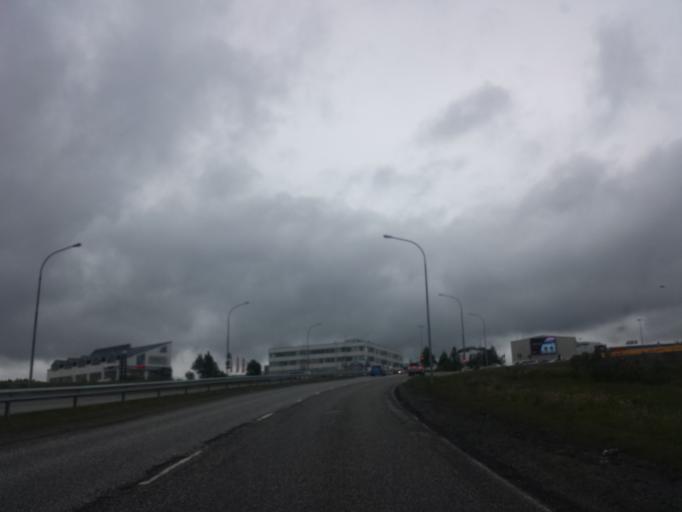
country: IS
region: Capital Region
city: Reykjavik
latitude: 64.1301
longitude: -21.8129
